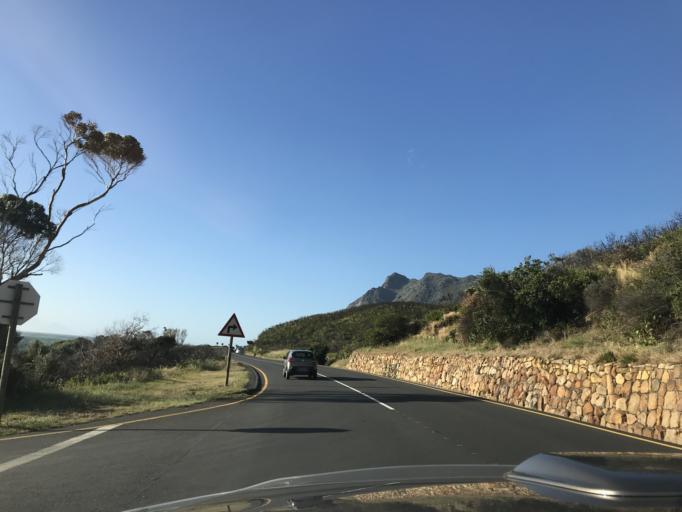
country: ZA
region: Western Cape
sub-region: Overberg District Municipality
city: Grabouw
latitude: -34.2505
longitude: 18.8562
